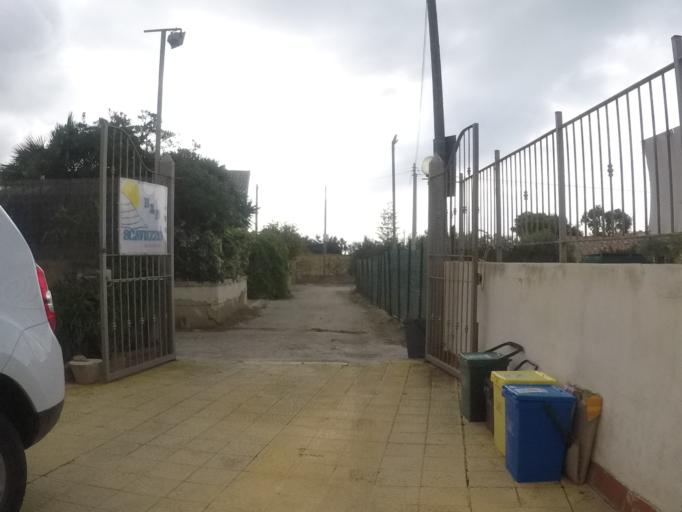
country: IT
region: Sicily
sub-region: Agrigento
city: Realmonte
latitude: 37.2900
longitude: 13.4786
